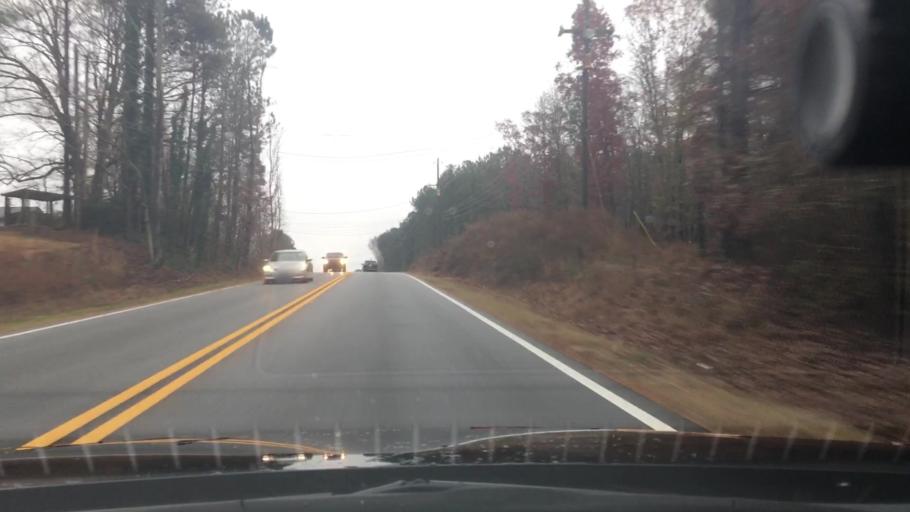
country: US
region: Georgia
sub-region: Fayette County
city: Peachtree City
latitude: 33.3957
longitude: -84.6787
